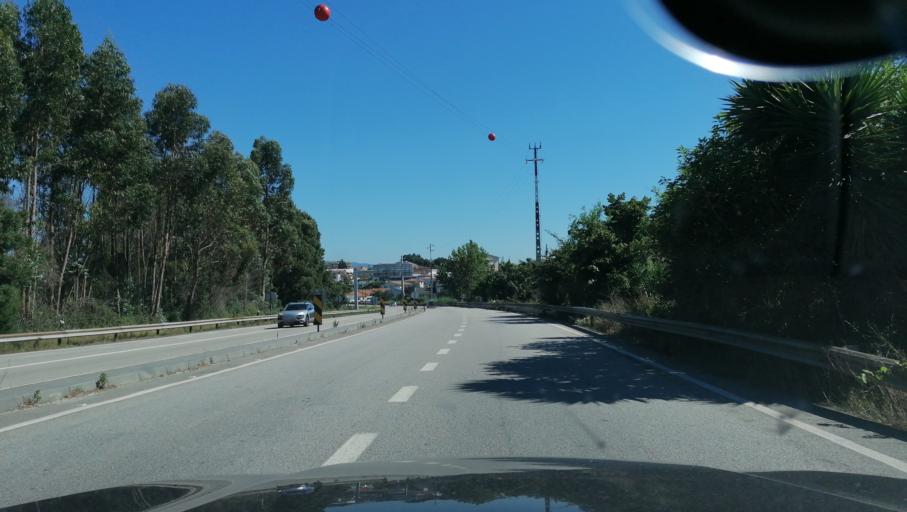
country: PT
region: Aveiro
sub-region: Santa Maria da Feira
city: Arrifana
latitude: 40.9236
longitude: -8.5023
